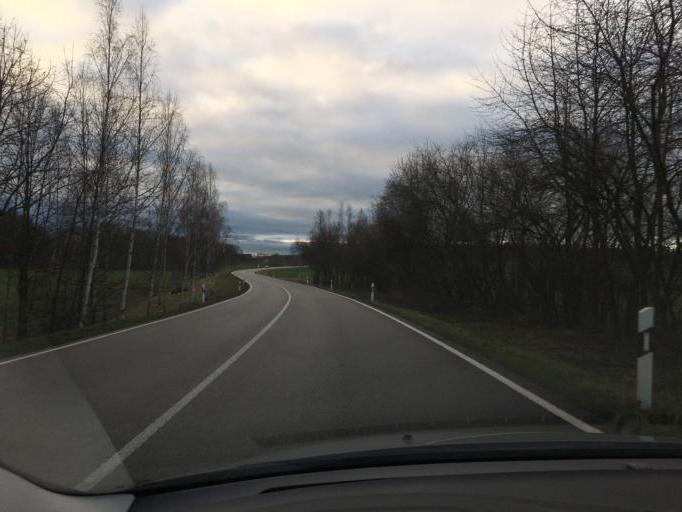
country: DE
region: Thuringia
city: Langenleuba-Niederhain
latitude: 51.0023
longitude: 12.5604
